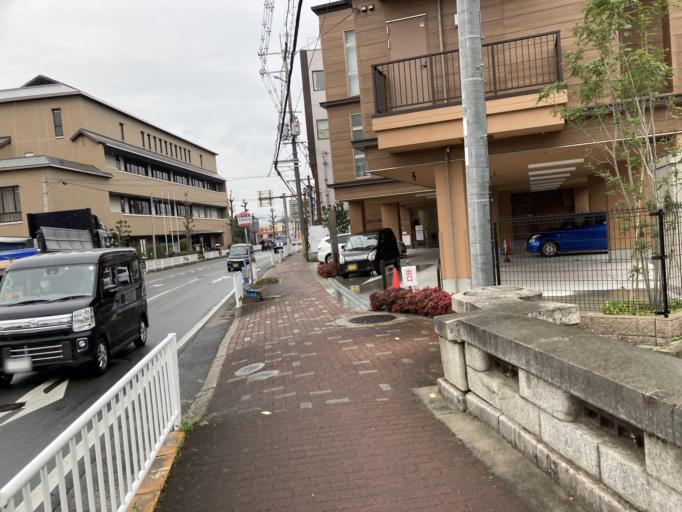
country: JP
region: Nara
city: Tenri
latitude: 34.5971
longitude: 135.8360
